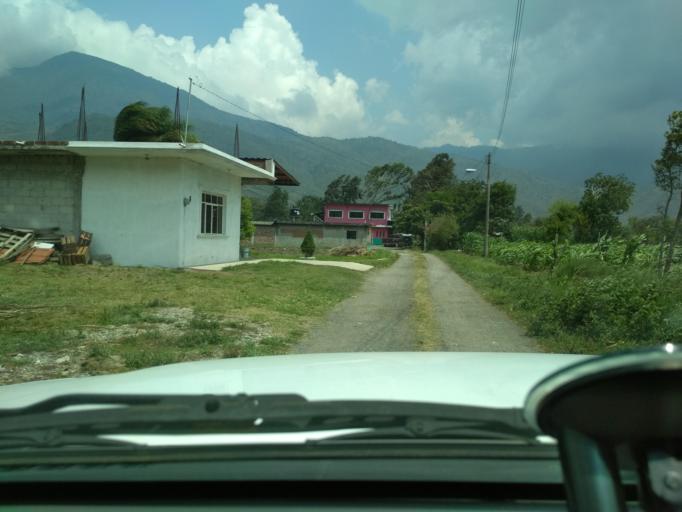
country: MX
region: Veracruz
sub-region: Nogales
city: Taza de Agua Ojo Zarco
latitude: 18.7779
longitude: -97.2192
